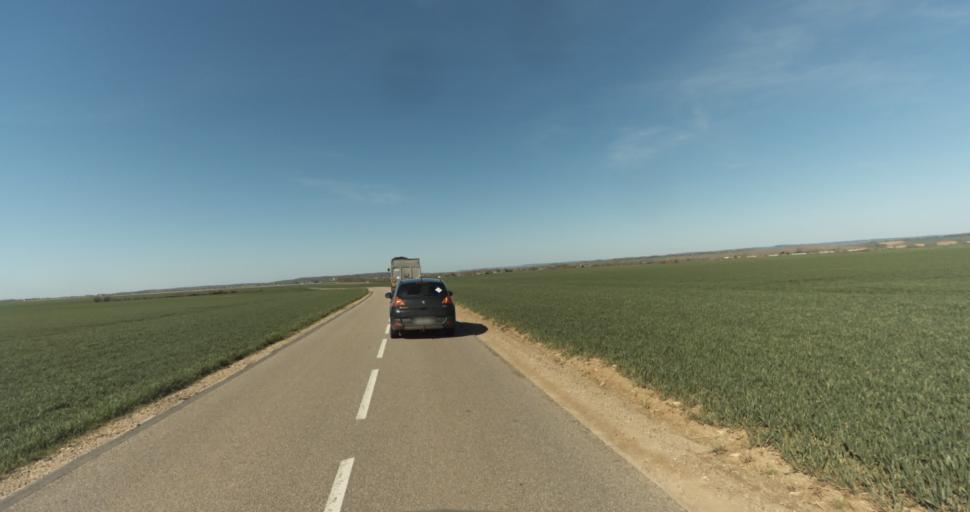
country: FR
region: Lower Normandy
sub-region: Departement du Calvados
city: Saint-Pierre-sur-Dives
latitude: 49.0374
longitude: -0.0648
